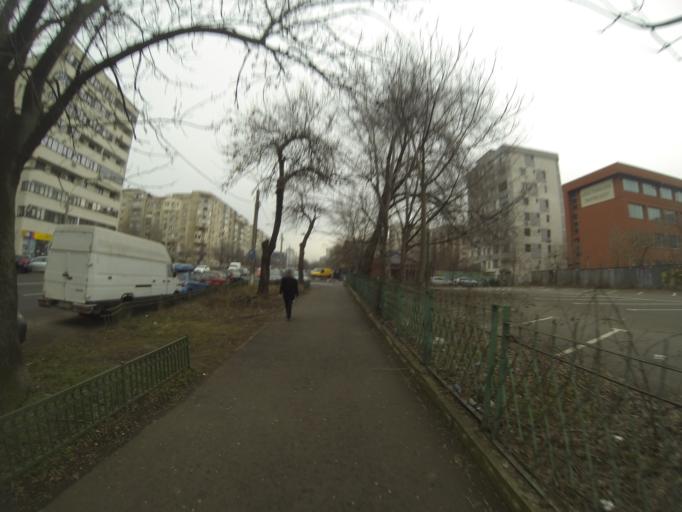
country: RO
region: Bucuresti
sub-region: Municipiul Bucuresti
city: Bucuresti
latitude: 44.4175
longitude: 26.0689
